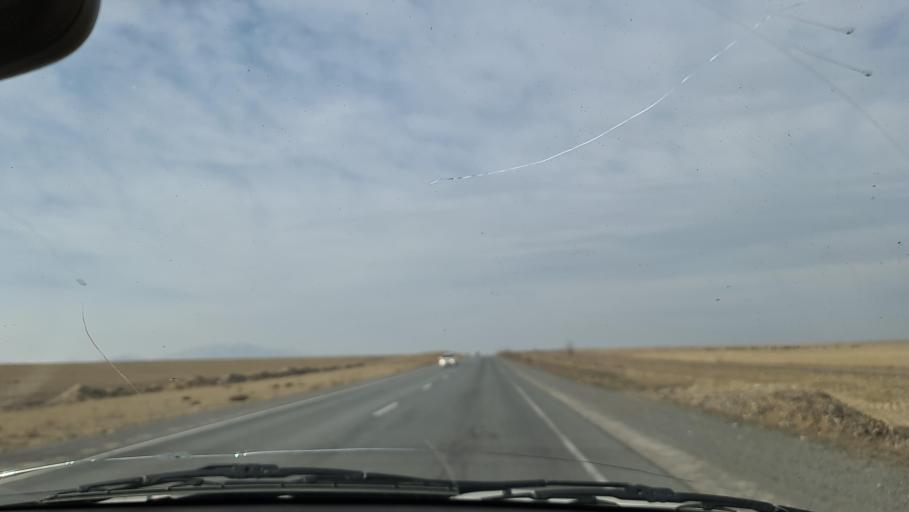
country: KG
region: Chuy
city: Bystrovka
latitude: 43.3220
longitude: 75.7198
